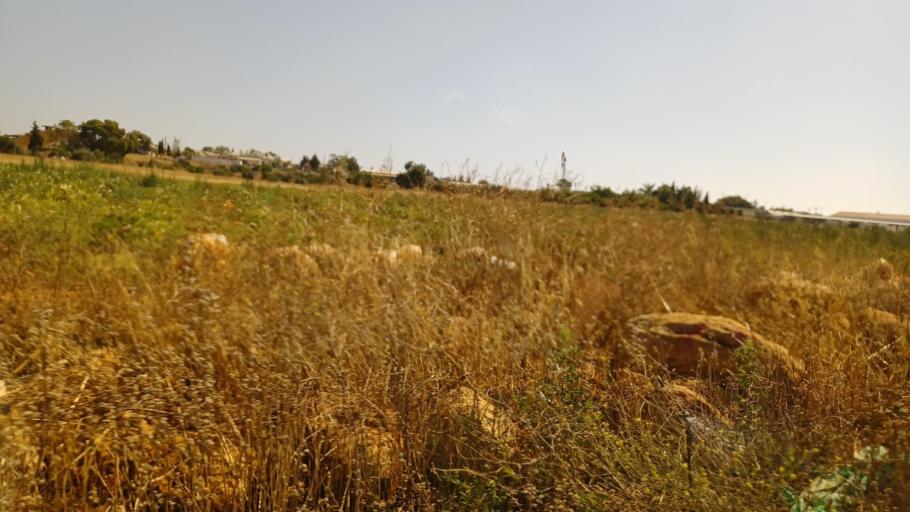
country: CY
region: Ammochostos
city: Frenaros
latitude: 35.0225
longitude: 33.9224
